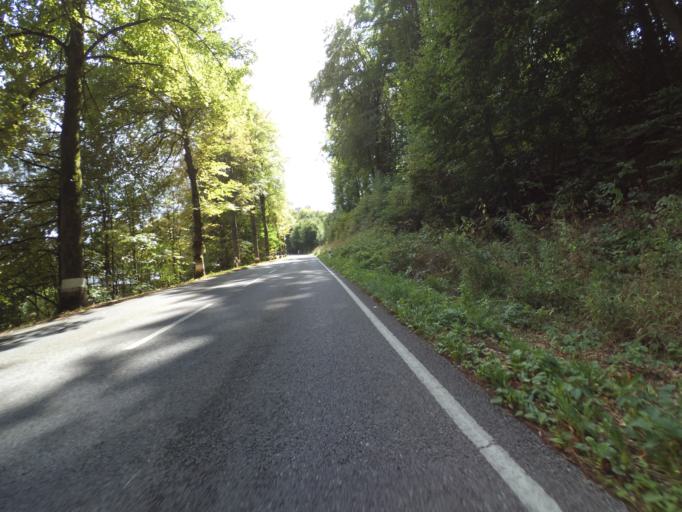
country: LU
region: Grevenmacher
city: Gonderange
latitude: 49.6620
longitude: 6.2281
